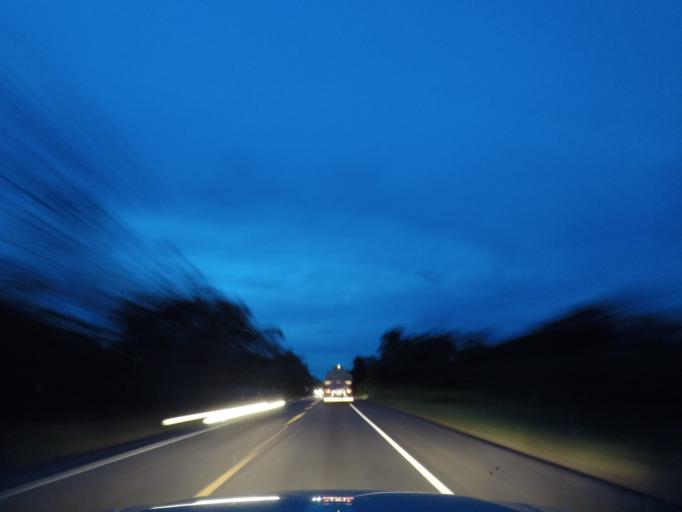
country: BR
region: Bahia
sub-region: Andarai
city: Vera Cruz
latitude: -12.4872
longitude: -41.3427
